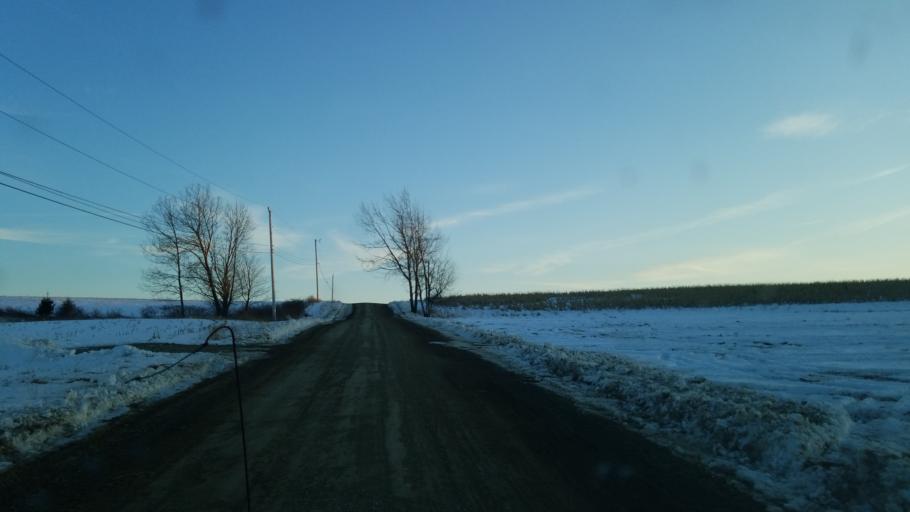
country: US
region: Pennsylvania
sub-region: Tioga County
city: Westfield
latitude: 42.0276
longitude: -77.6196
